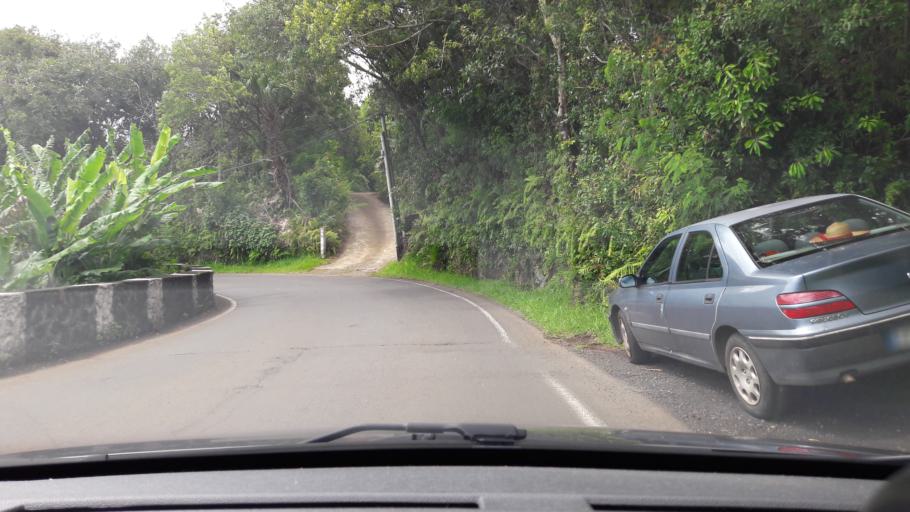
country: RE
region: Reunion
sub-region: Reunion
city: Saint-Benoit
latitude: -21.0904
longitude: 55.7018
